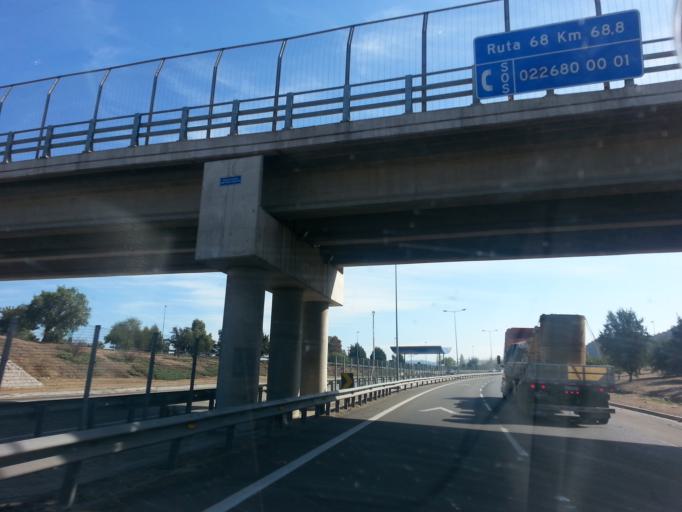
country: CL
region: Valparaiso
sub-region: Provincia de Marga Marga
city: Quilpue
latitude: -33.3299
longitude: -71.3890
